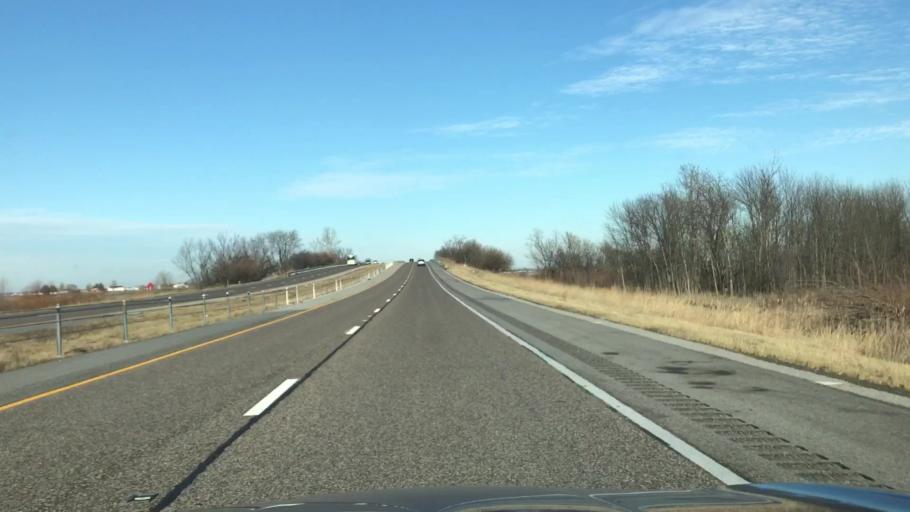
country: US
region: Illinois
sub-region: Madison County
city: Edwardsville
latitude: 38.8215
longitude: -89.8855
